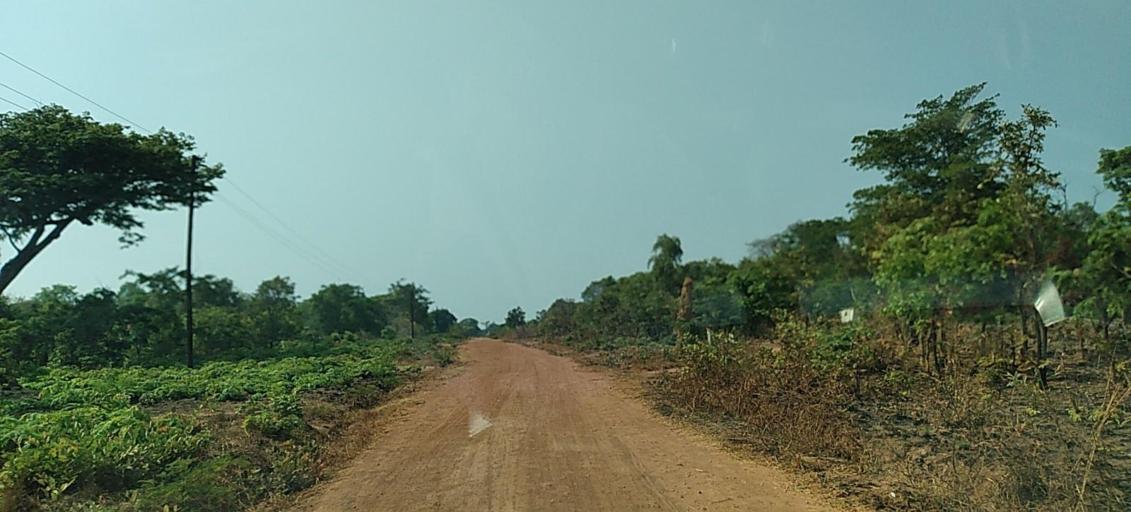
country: ZM
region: Copperbelt
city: Chingola
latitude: -12.9117
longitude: 27.3724
